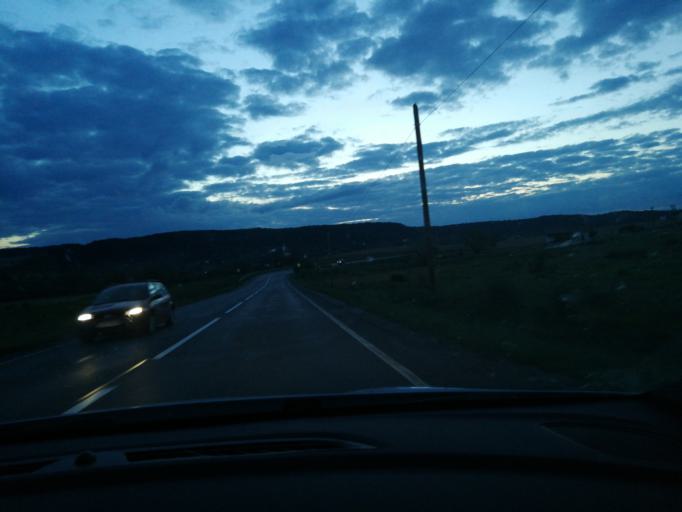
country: RO
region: Brasov
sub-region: Comuna Bunesti
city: Bunesti
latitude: 46.1179
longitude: 25.0310
